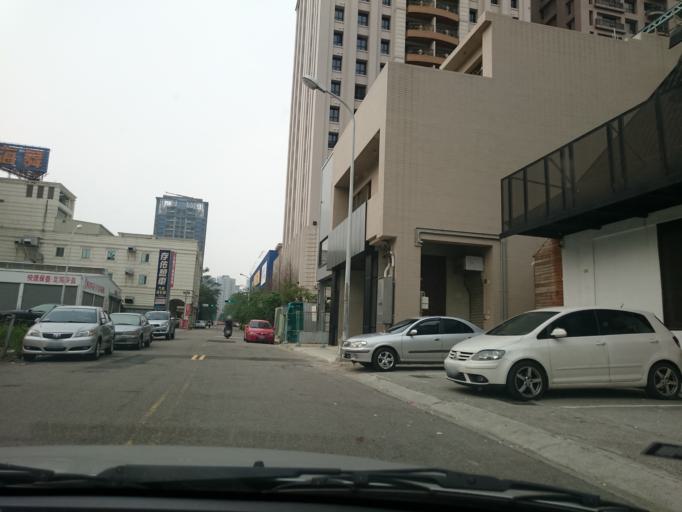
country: TW
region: Taiwan
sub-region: Taichung City
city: Taichung
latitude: 24.1458
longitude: 120.6425
